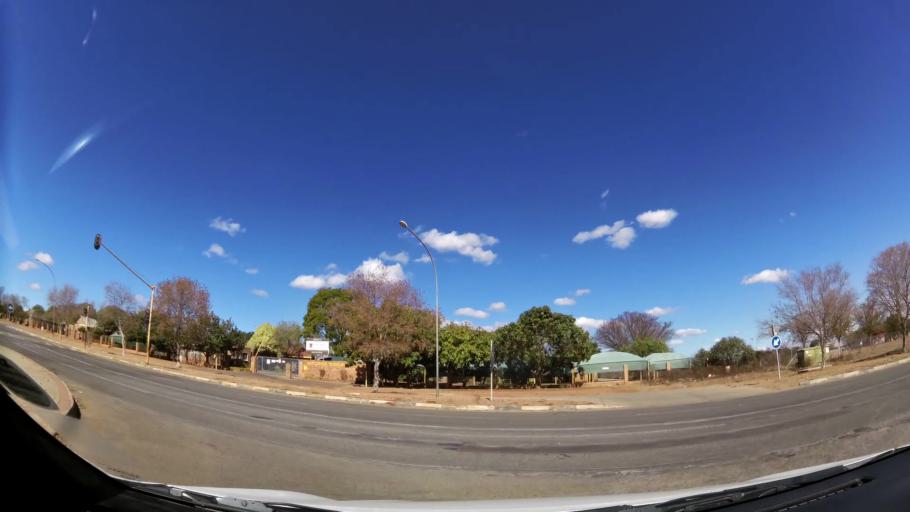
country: ZA
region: Limpopo
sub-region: Capricorn District Municipality
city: Polokwane
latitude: -23.9168
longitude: 29.4790
